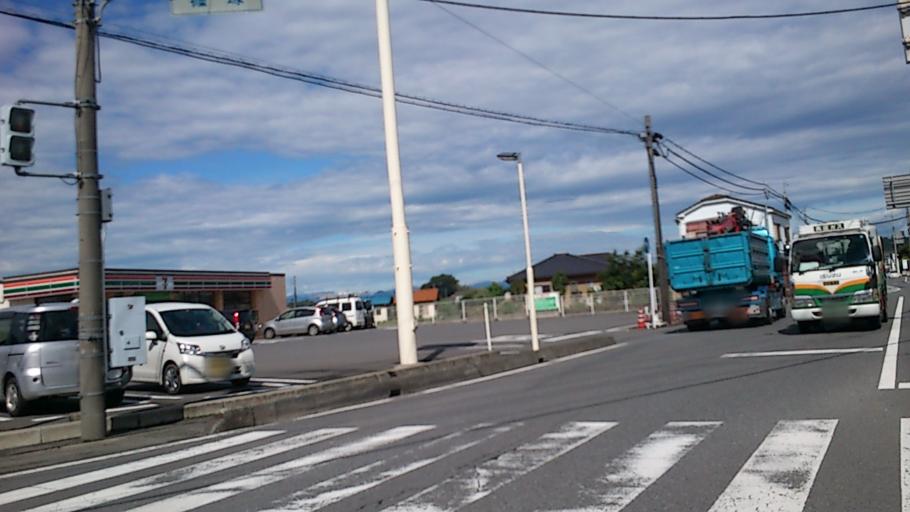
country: JP
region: Gunma
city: Fujioka
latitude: 36.2632
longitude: 139.0581
